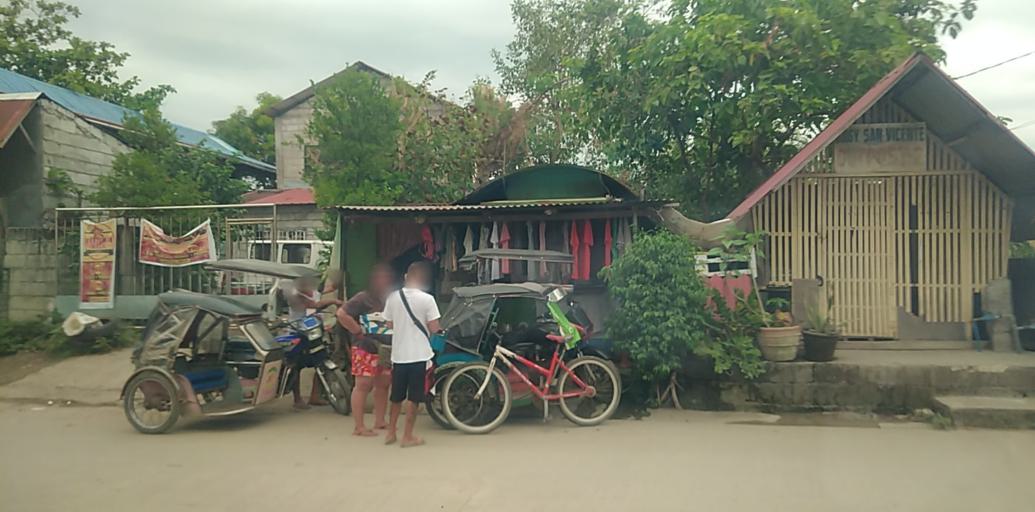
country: PH
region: Central Luzon
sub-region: Province of Pampanga
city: San Fernando
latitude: 15.0030
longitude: 120.7021
